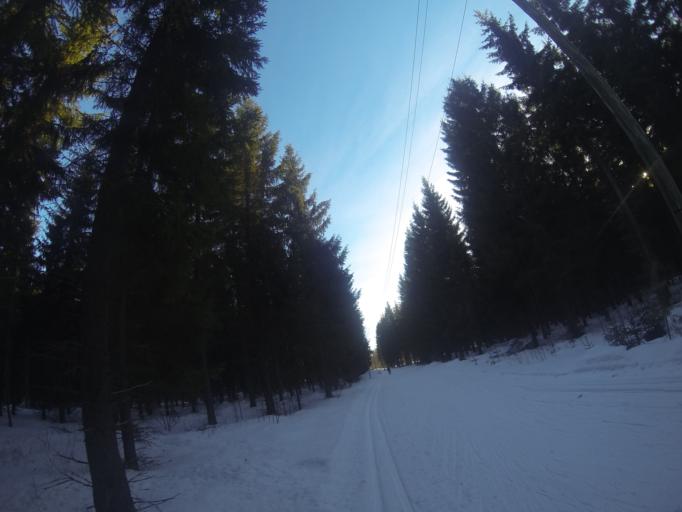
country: FI
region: Southern Savonia
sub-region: Savonlinna
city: Savonlinna
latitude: 61.9259
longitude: 28.8963
